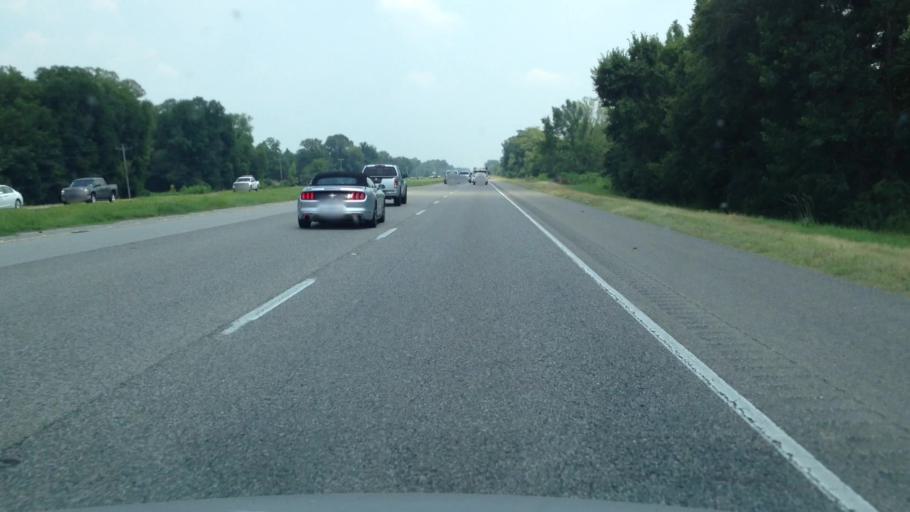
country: US
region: Louisiana
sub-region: West Baton Rouge Parish
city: Erwinville
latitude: 30.5176
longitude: -91.3618
